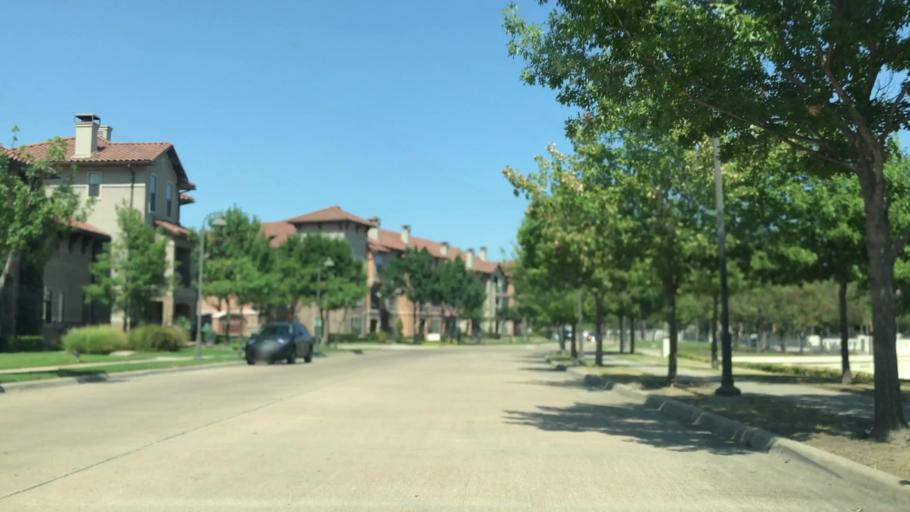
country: US
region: Texas
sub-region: Dallas County
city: Farmers Branch
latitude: 32.8998
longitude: -96.9393
